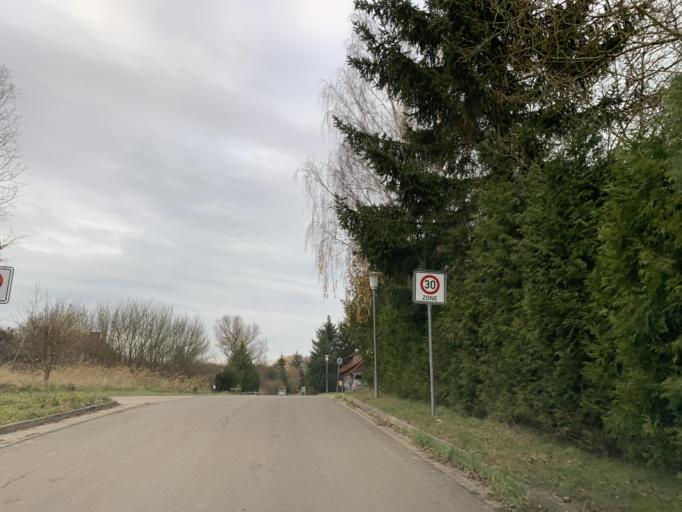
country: DE
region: Mecklenburg-Vorpommern
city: Carpin
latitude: 53.4027
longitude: 13.2011
